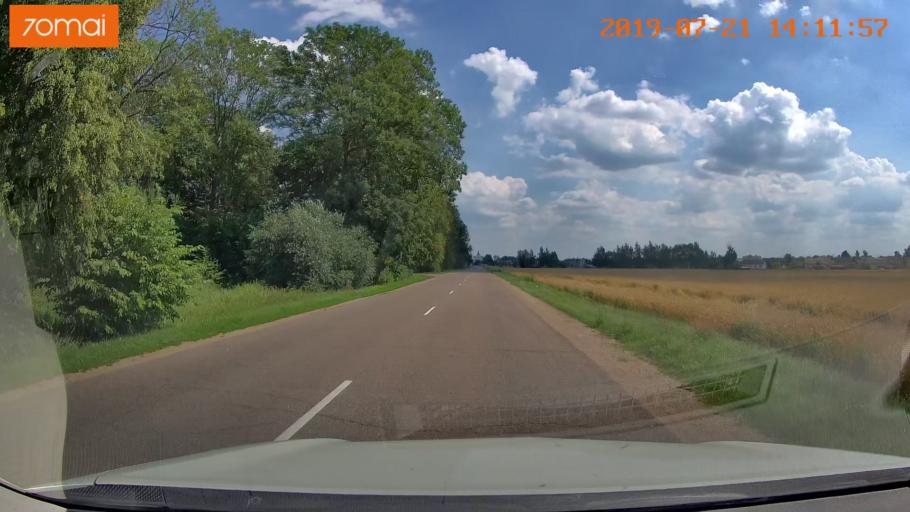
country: BY
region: Grodnenskaya
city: Karelichy
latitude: 53.6546
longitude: 26.1617
